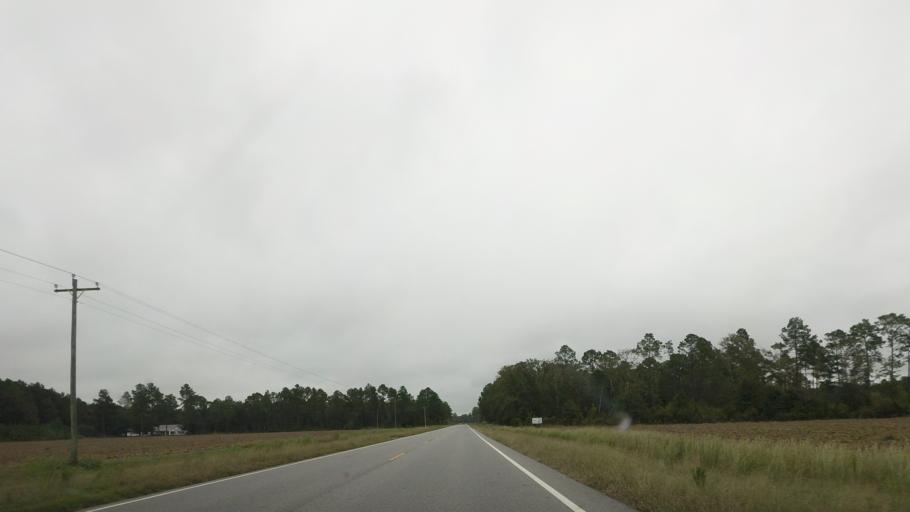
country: US
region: Georgia
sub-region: Berrien County
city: Nashville
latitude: 31.2898
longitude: -83.2377
